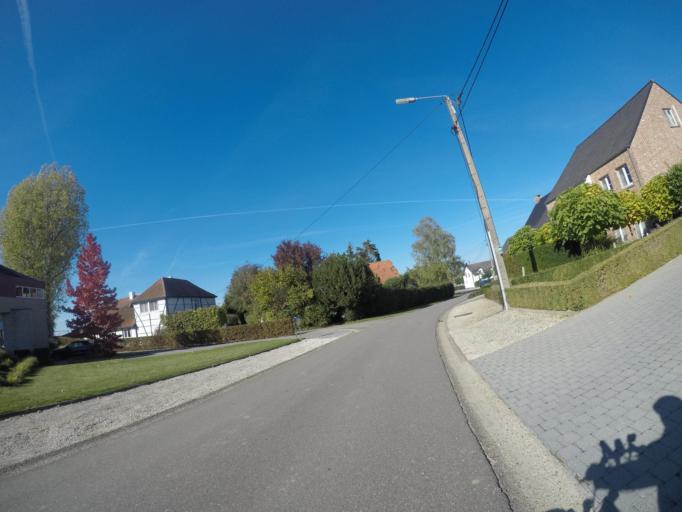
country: BE
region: Flanders
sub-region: Provincie Limburg
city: Alken
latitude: 50.8779
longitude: 5.2585
